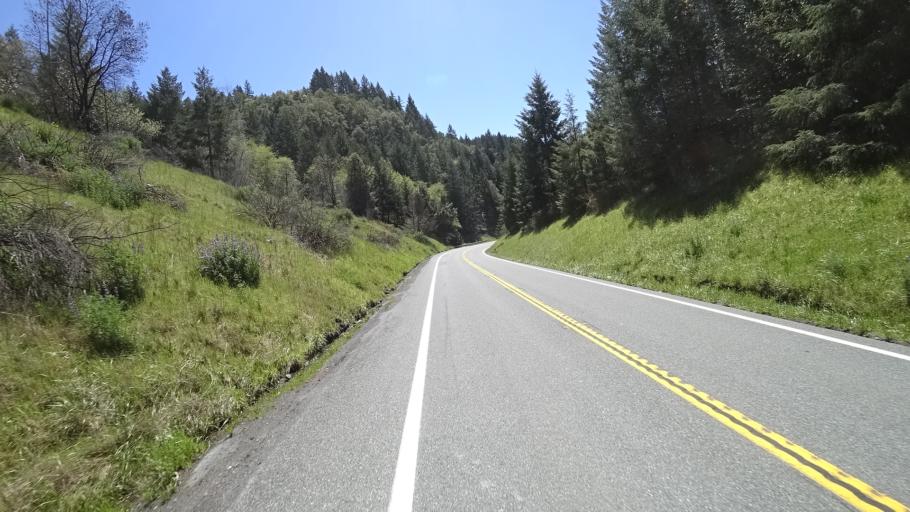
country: US
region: California
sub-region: Humboldt County
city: Willow Creek
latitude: 40.9210
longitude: -123.7947
